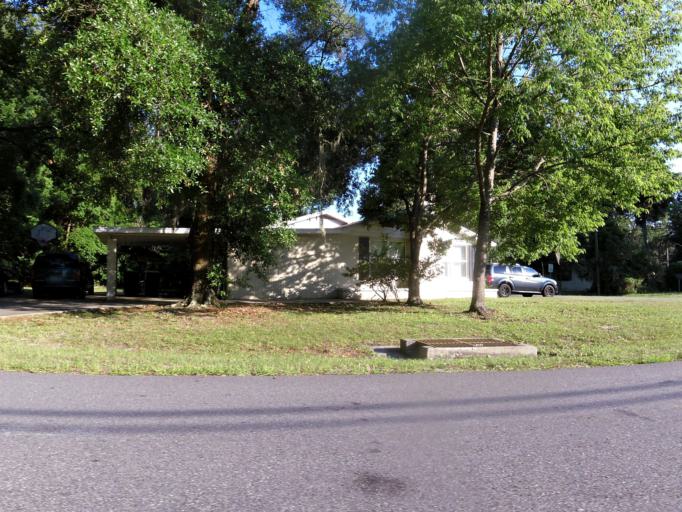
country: US
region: Florida
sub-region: Duval County
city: Jacksonville
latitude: 30.2379
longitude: -81.6199
